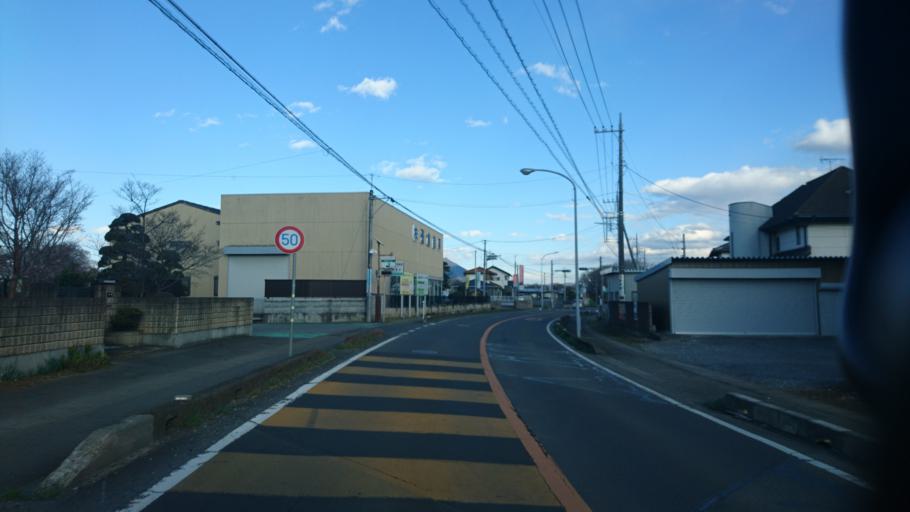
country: JP
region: Ibaraki
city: Shimodate
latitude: 36.2470
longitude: 139.9646
